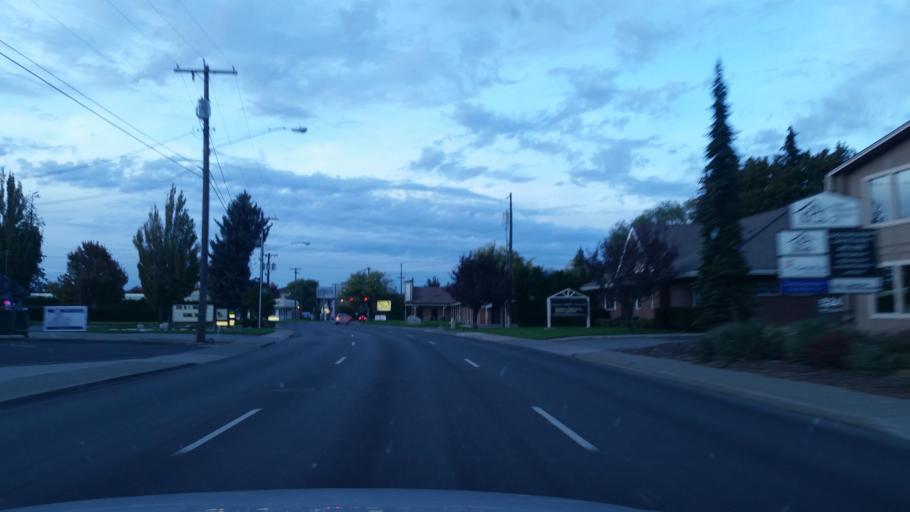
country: US
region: Washington
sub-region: Spokane County
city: Dishman
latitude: 47.6623
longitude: -117.2815
